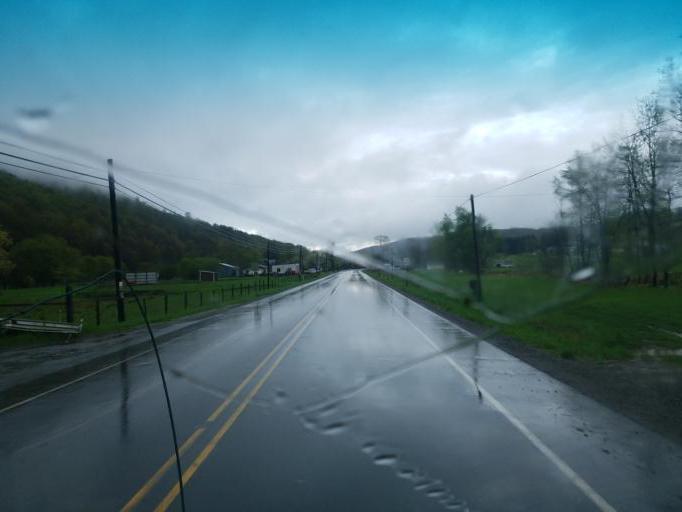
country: US
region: Pennsylvania
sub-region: Tioga County
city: Westfield
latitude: 41.9346
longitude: -77.6372
